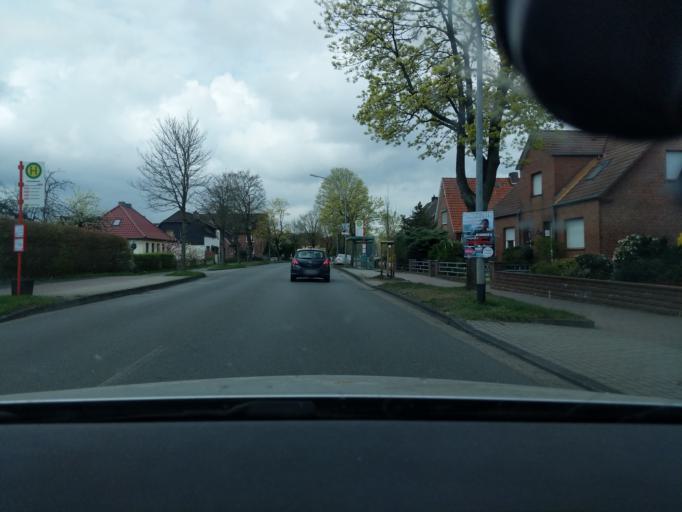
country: DE
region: Lower Saxony
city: Stade
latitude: 53.5863
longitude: 9.4919
